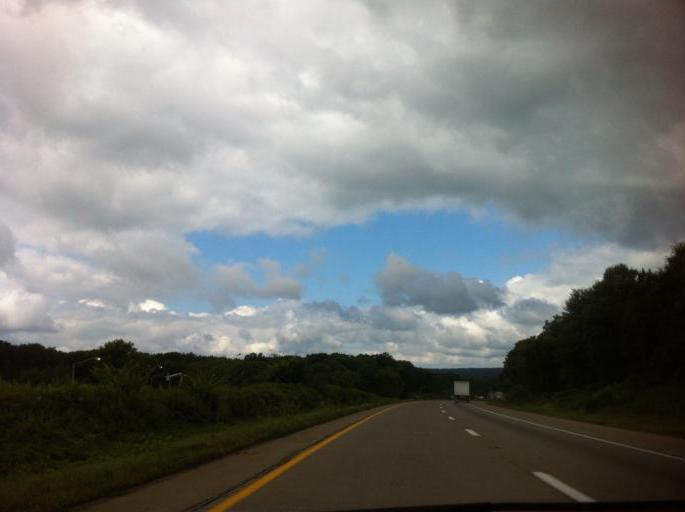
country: US
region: Pennsylvania
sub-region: Mercer County
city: Farrell
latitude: 41.1811
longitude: -80.4989
